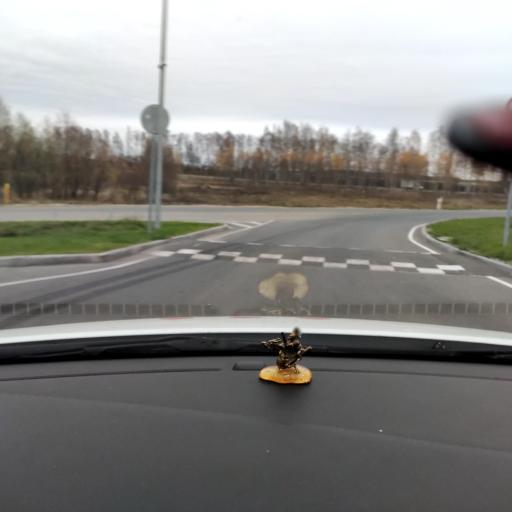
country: RU
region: Tatarstan
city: Osinovo
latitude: 55.8621
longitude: 48.8354
